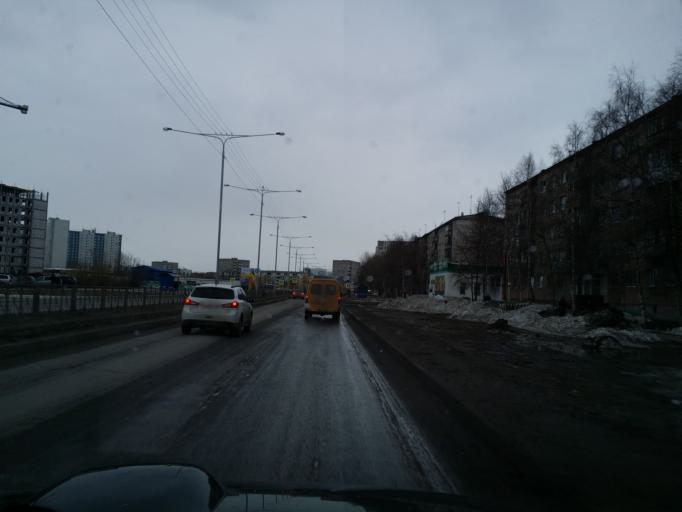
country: RU
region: Khanty-Mansiyskiy Avtonomnyy Okrug
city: Nizhnevartovsk
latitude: 60.9495
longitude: 76.5631
